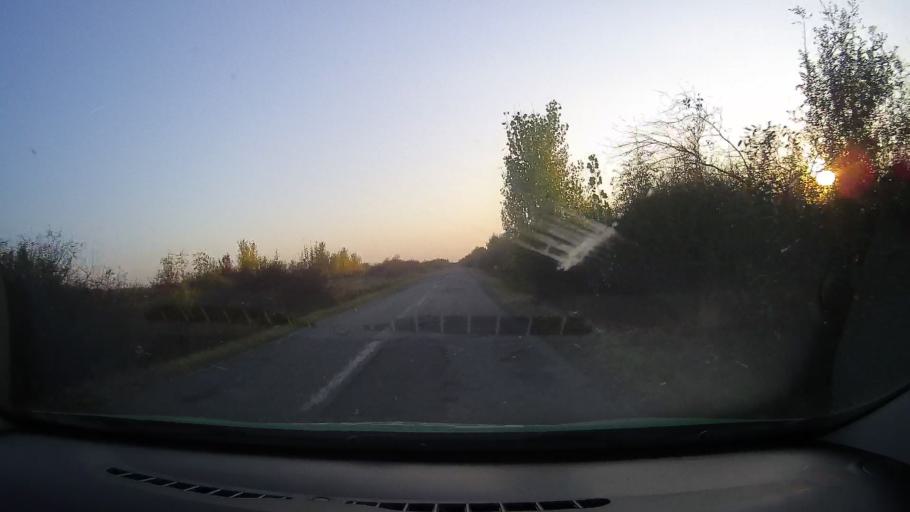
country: RO
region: Arad
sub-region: Comuna Sicula
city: Sicula
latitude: 46.4093
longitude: 21.7320
